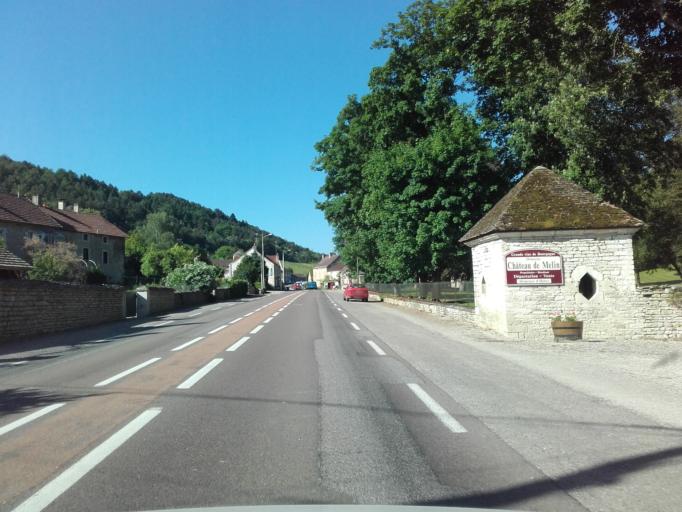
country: FR
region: Bourgogne
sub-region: Departement de la Cote-d'Or
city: Meursault
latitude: 46.9821
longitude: 4.7118
